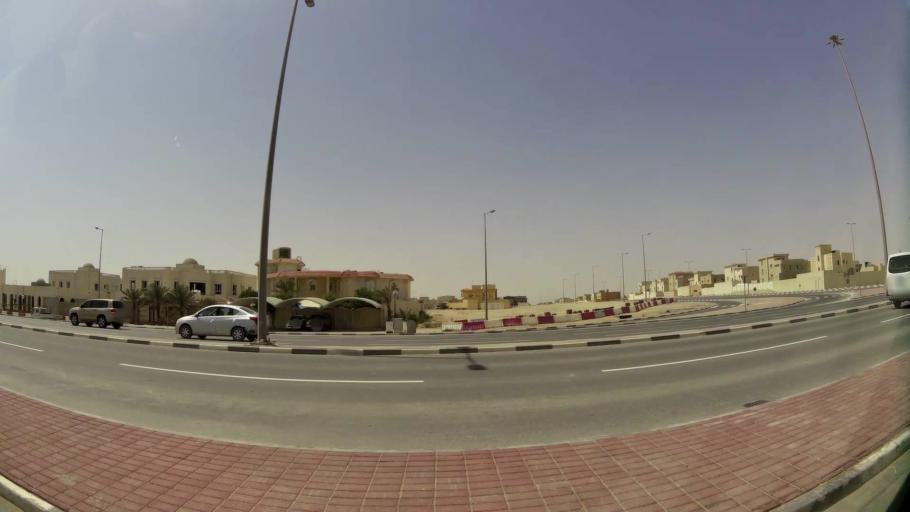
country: QA
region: Baladiyat Umm Salal
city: Umm Salal Muhammad
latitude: 25.4043
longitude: 51.4556
